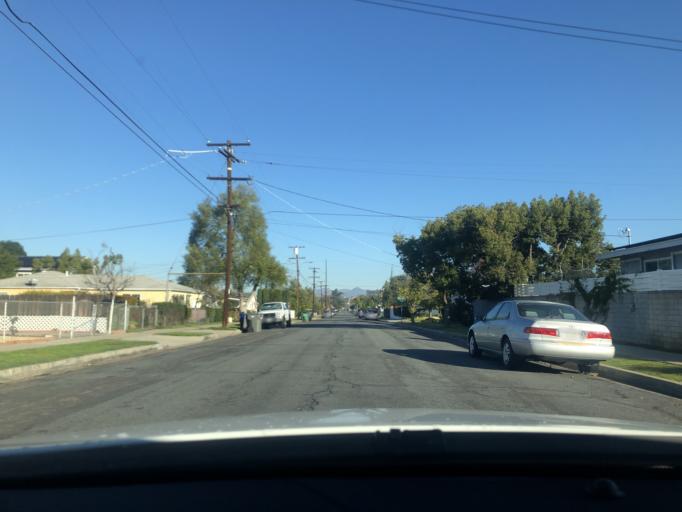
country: US
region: California
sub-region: San Diego County
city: El Cajon
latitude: 32.7821
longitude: -116.9600
